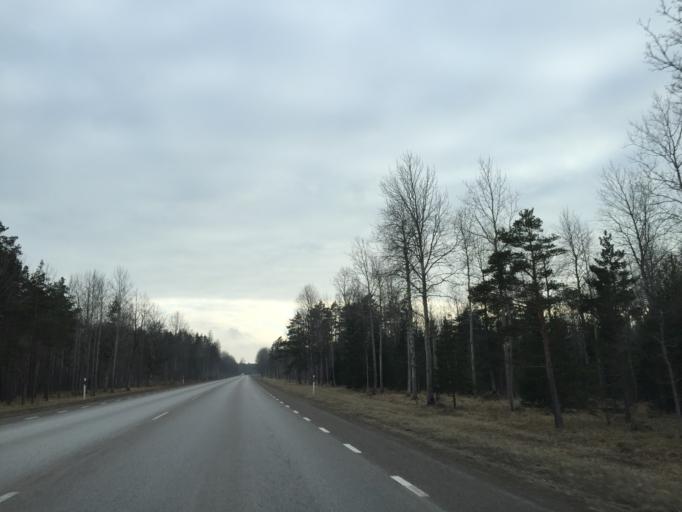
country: EE
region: Saare
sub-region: Orissaare vald
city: Orissaare
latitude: 58.4605
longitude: 22.8110
